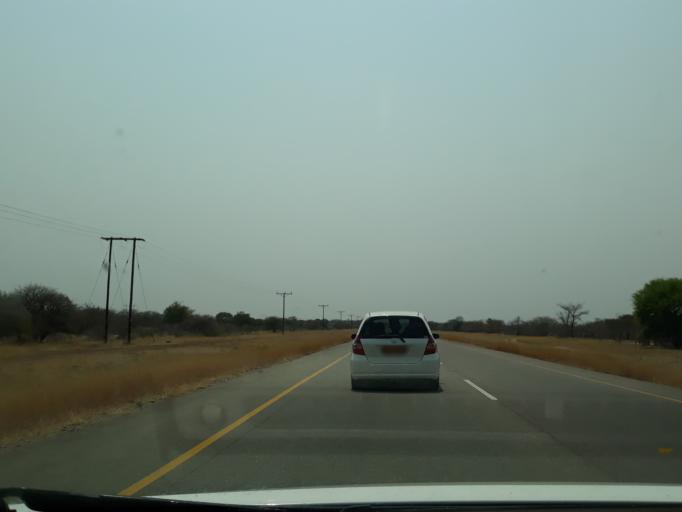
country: BW
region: Kgatleng
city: Mochudi
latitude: -24.3032
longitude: 26.1239
